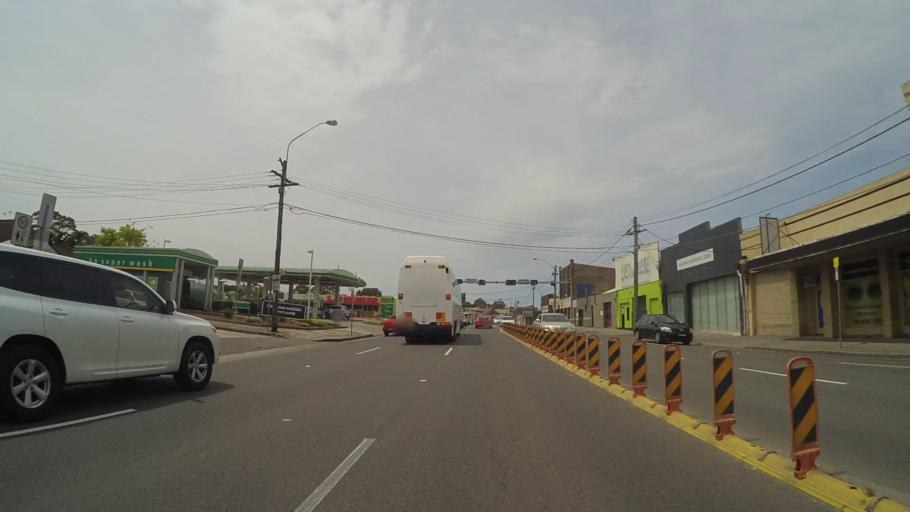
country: AU
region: New South Wales
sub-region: Marrickville
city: Newtown
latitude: -33.9168
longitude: 151.1725
